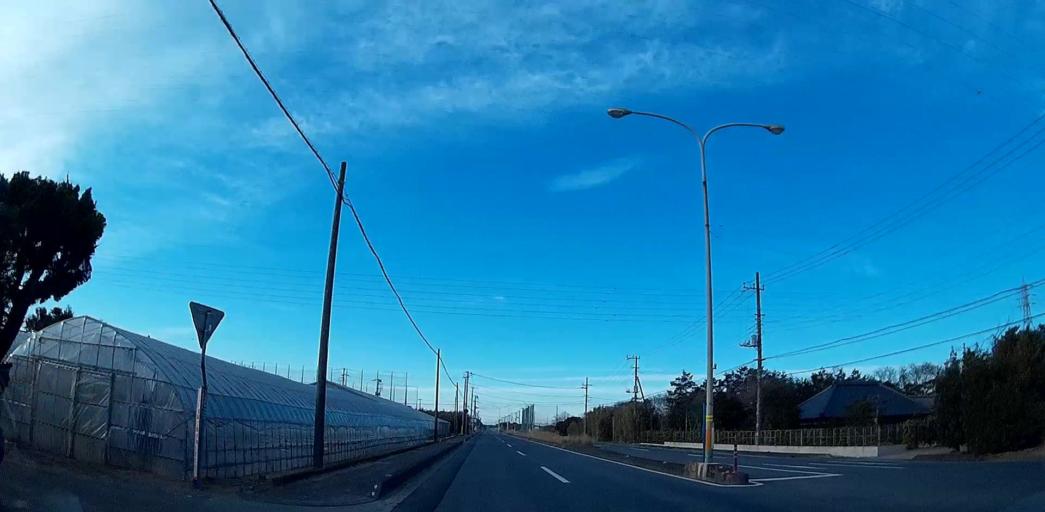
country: JP
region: Chiba
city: Hasaki
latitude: 35.8129
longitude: 140.7392
